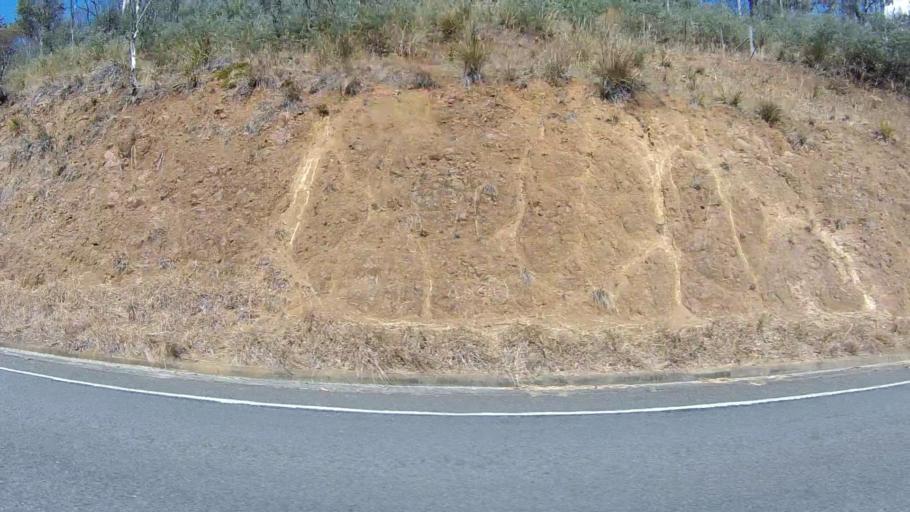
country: AU
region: Tasmania
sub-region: Sorell
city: Sorell
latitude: -42.6070
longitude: 147.6457
